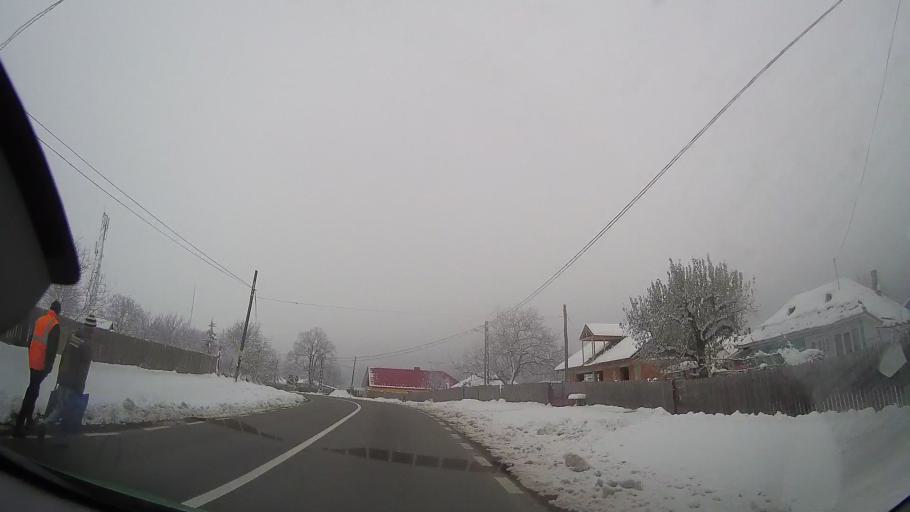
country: RO
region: Neamt
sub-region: Comuna Poenari
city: Poienari
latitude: 46.8793
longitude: 27.1322
